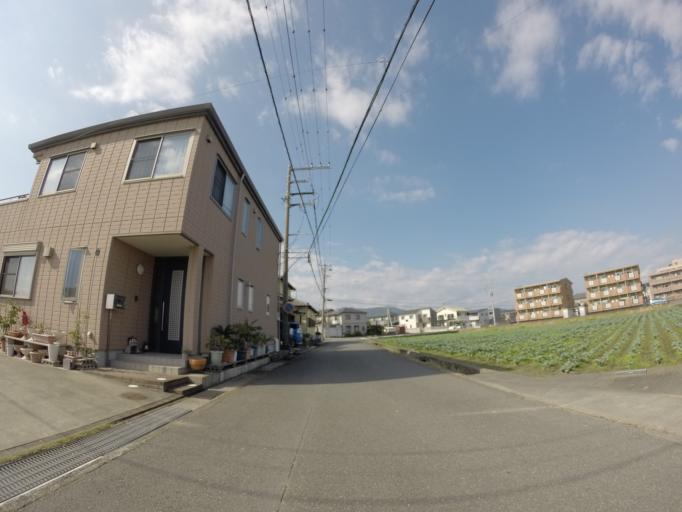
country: JP
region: Shizuoka
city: Fuji
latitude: 35.1321
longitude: 138.6645
